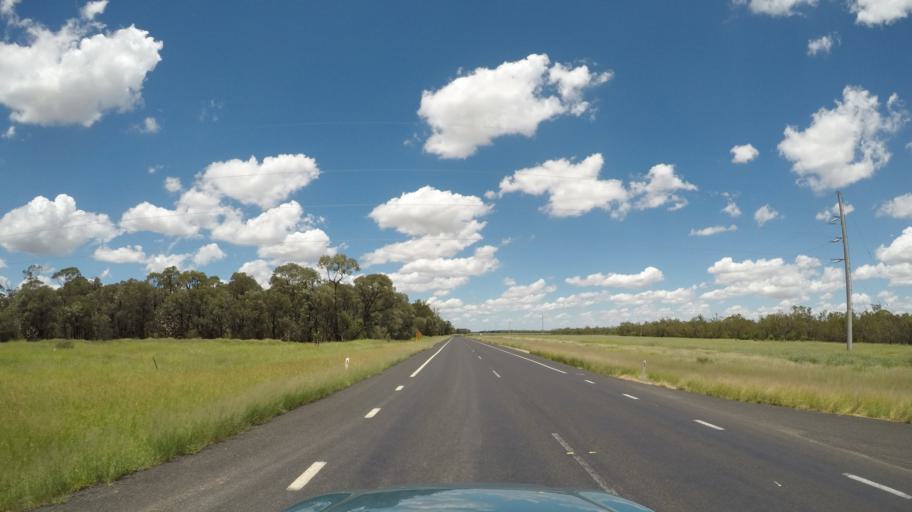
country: AU
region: Queensland
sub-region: Goondiwindi
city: Goondiwindi
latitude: -28.1094
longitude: 150.7192
